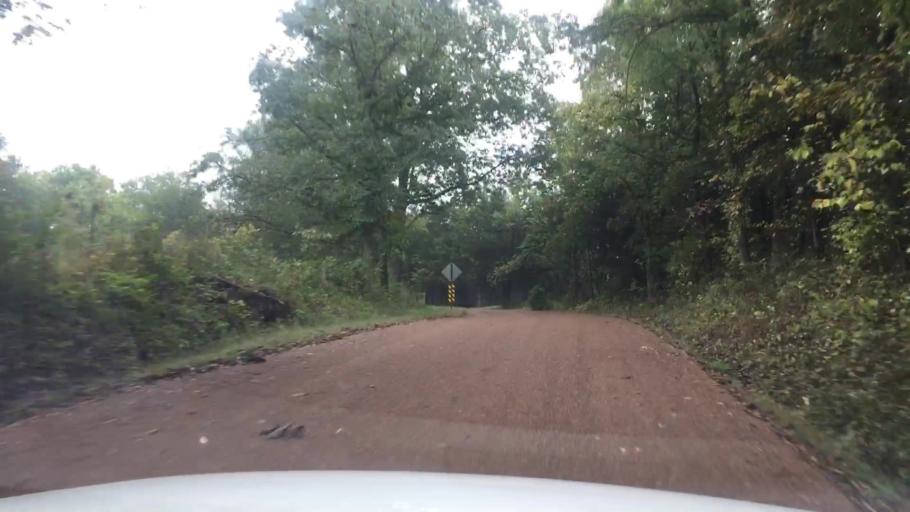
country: US
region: Missouri
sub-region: Boone County
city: Ashland
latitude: 38.8210
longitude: -92.3271
